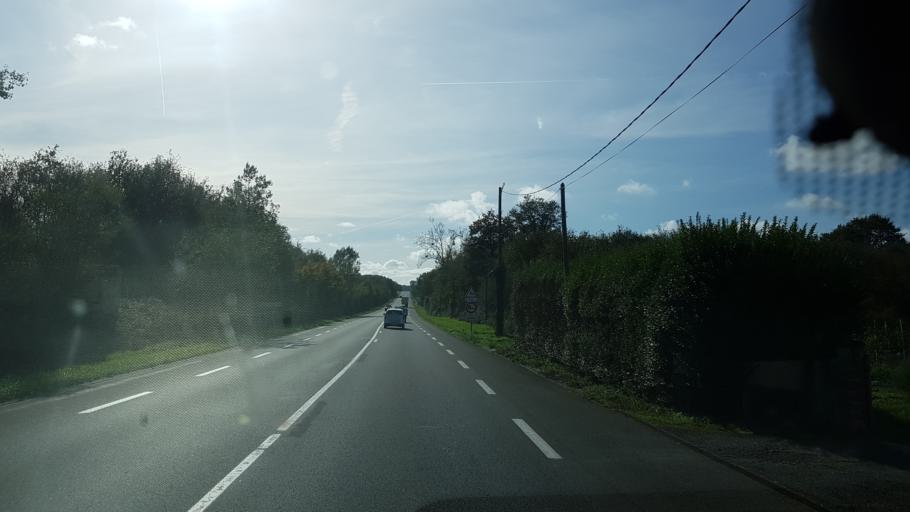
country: FR
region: Poitou-Charentes
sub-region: Departement de la Charente
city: Loubert
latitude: 45.9307
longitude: 0.5286
